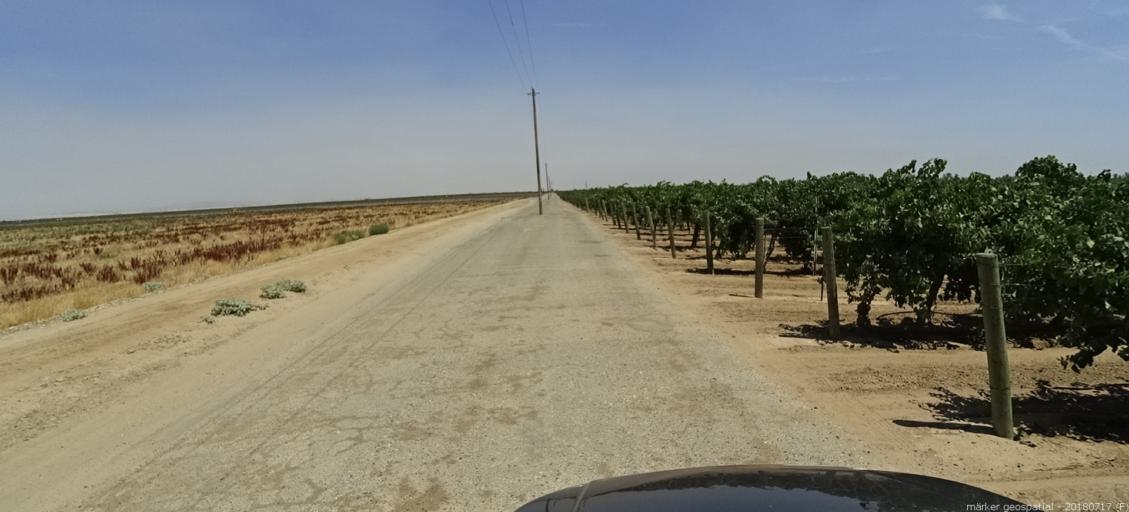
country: US
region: California
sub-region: Madera County
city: Fairmead
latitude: 37.0690
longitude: -120.1235
